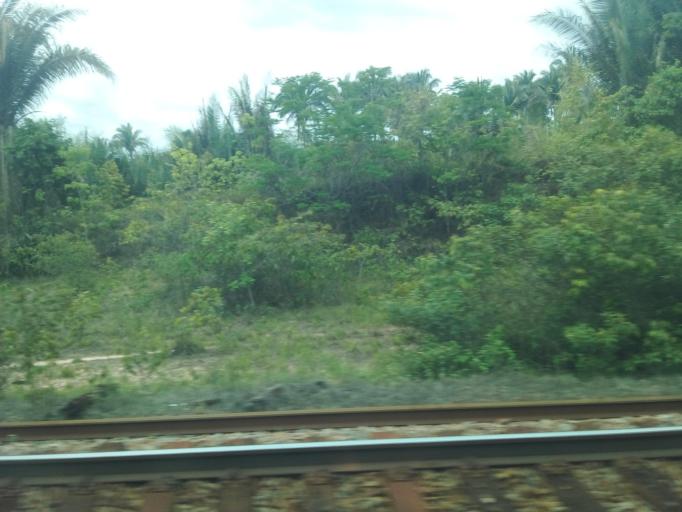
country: BR
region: Maranhao
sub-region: Santa Ines
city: Santa Ines
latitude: -3.6526
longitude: -45.7947
